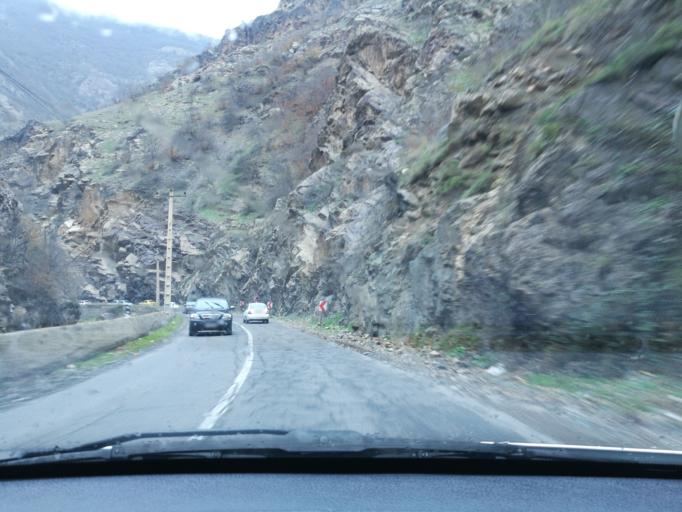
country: IR
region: Mazandaran
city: Chalus
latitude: 36.2881
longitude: 51.2421
